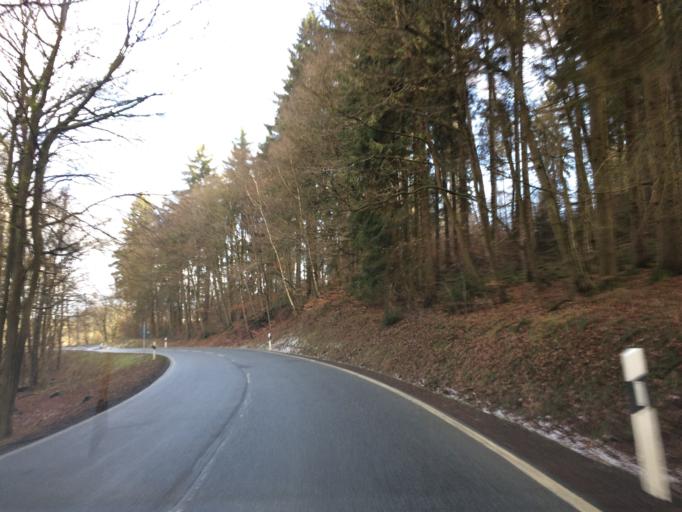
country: DE
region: Hesse
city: Bad Camberg
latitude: 50.3298
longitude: 8.3379
